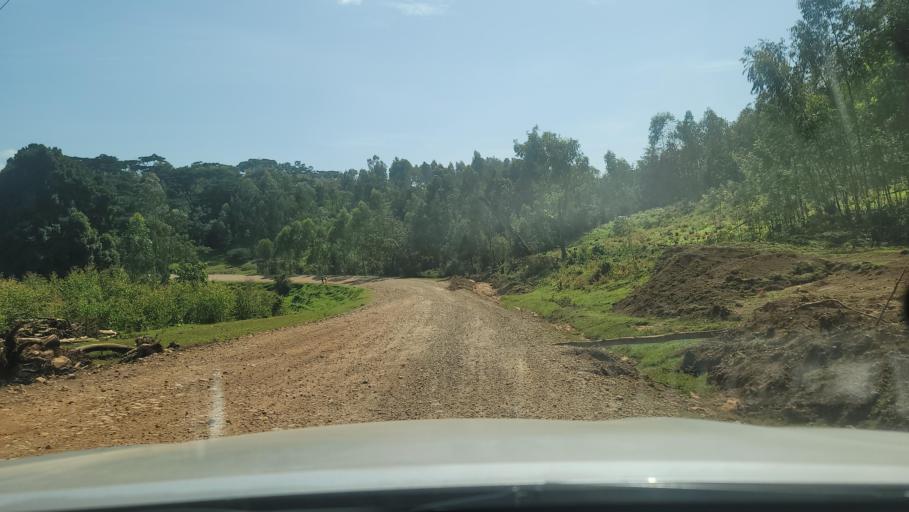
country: ET
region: Oromiya
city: Agaro
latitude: 7.7968
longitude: 36.4562
